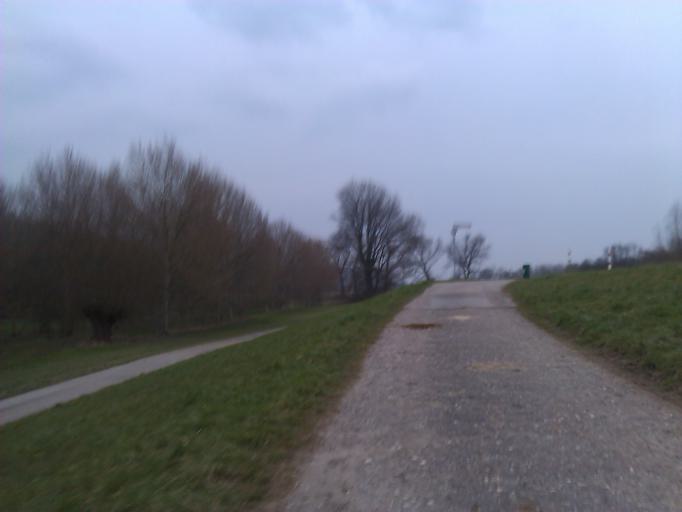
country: DE
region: North Rhine-Westphalia
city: Monheim am Rhein
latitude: 51.1103
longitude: 6.8707
